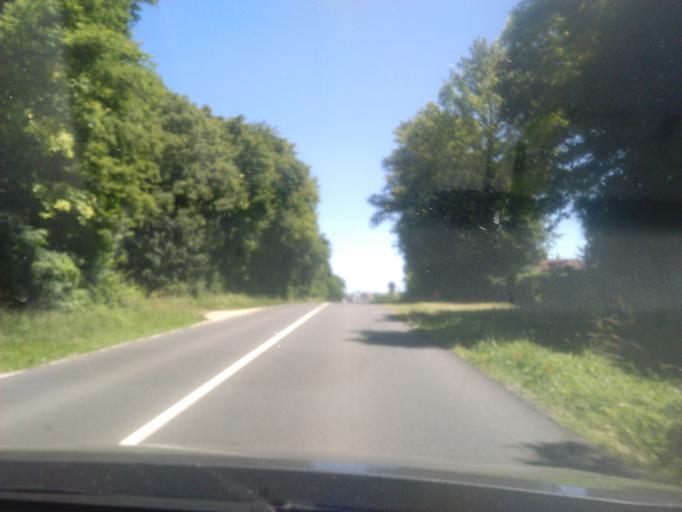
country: FR
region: Centre
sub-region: Departement du Loir-et-Cher
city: Saint-Sulpice-de-Pommeray
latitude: 47.6144
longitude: 1.2296
